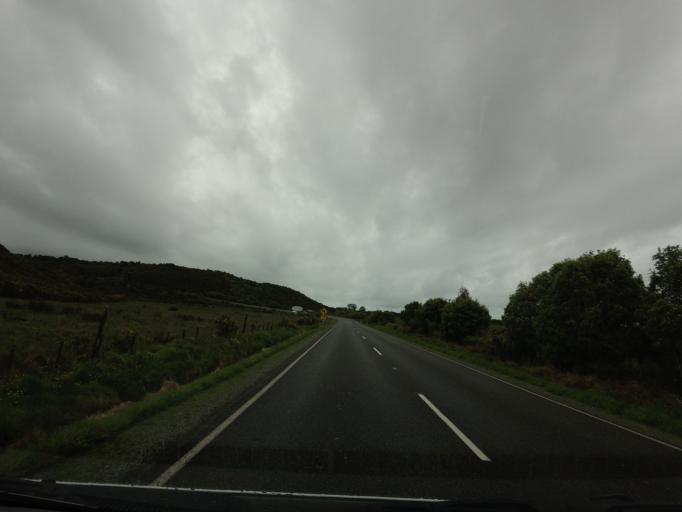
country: NZ
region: West Coast
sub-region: Westland District
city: Hokitika
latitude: -42.8892
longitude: 170.8289
